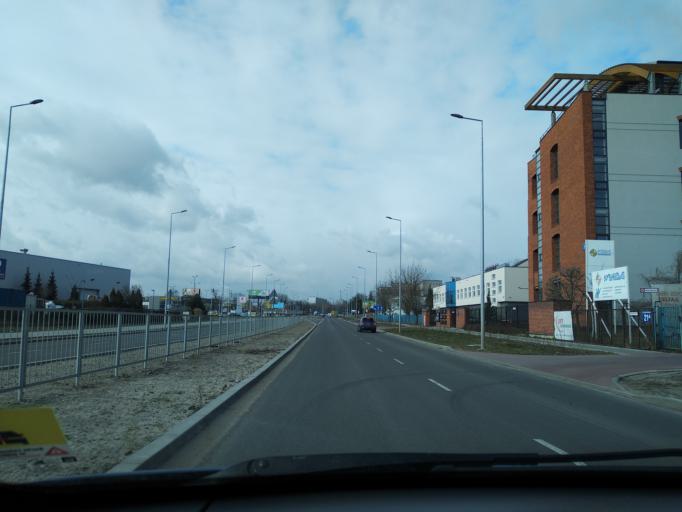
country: PL
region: Masovian Voivodeship
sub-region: Powiat piaseczynski
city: Piaseczno
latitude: 52.0826
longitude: 21.0295
